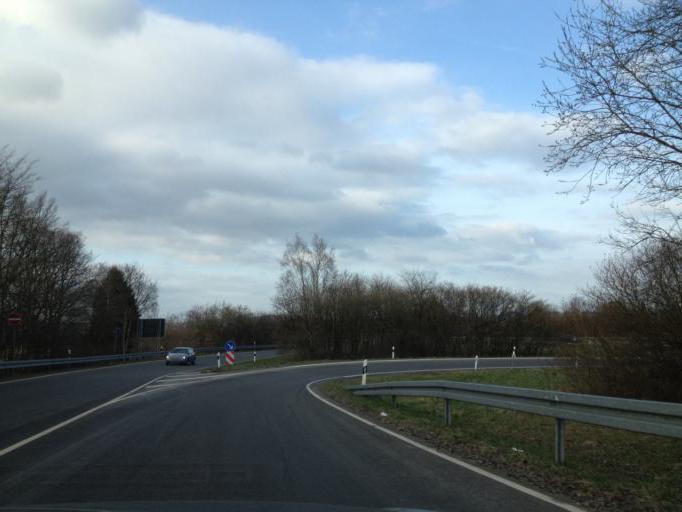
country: DE
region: Saarland
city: Sankt Wendel
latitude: 49.4698
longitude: 7.1482
